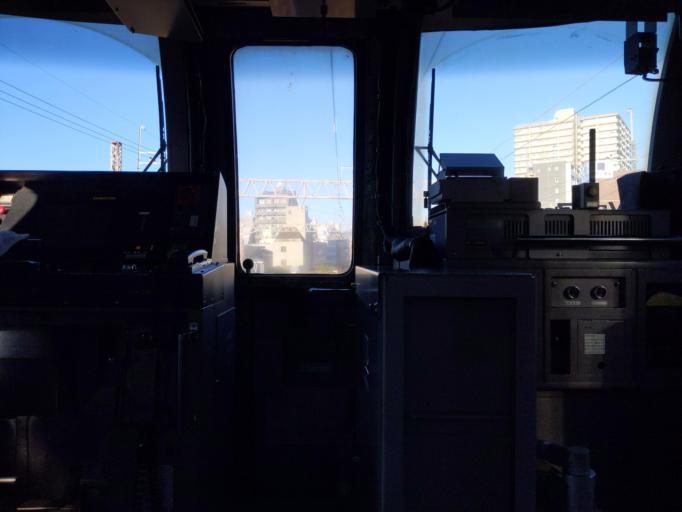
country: JP
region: Tokyo
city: Urayasu
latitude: 35.7047
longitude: 139.8401
